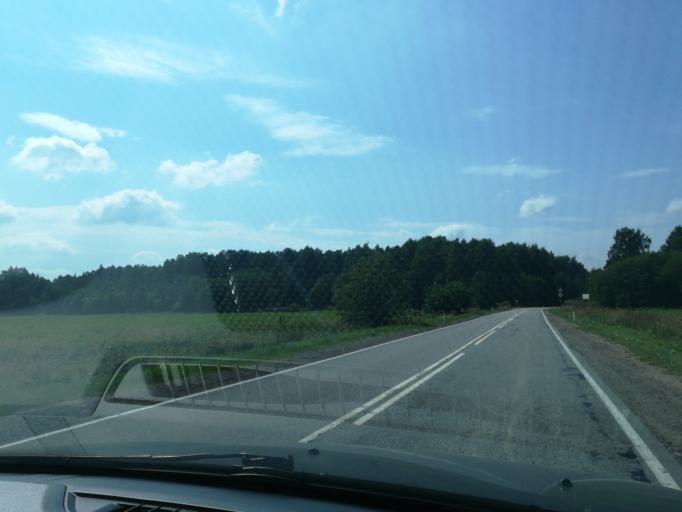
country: RU
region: Leningrad
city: Sista-Palkino
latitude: 59.5838
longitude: 28.8141
